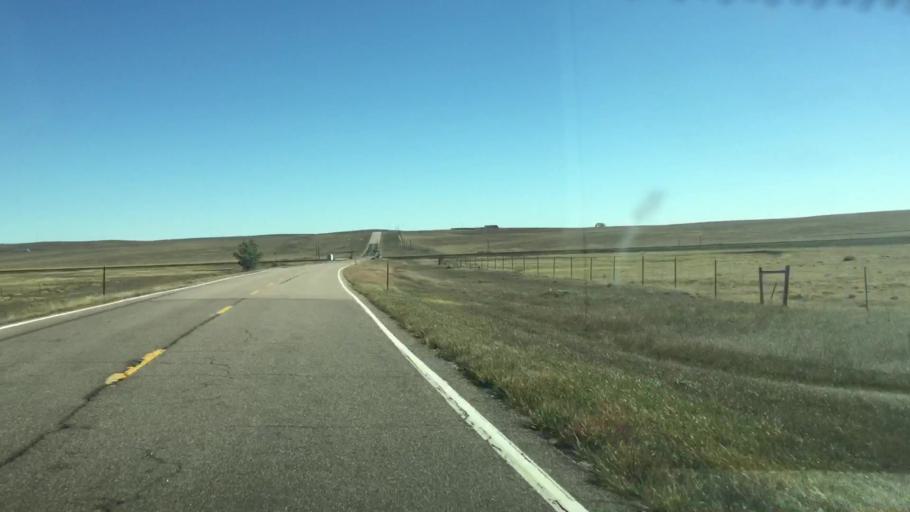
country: US
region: Colorado
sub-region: Lincoln County
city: Limon
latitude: 39.3064
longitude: -103.8394
